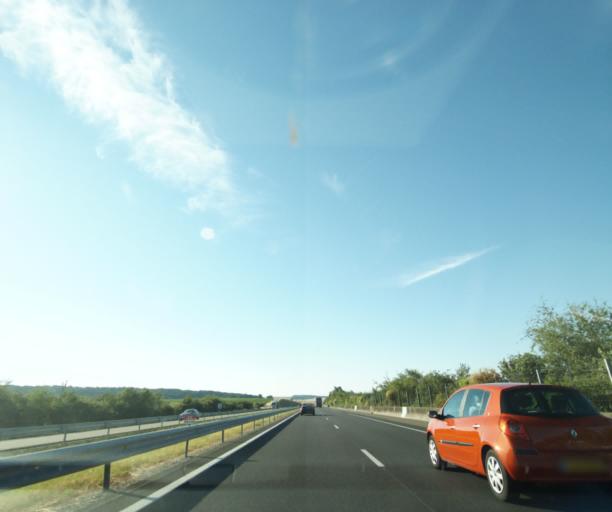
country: FR
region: Bourgogne
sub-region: Departement de l'Yonne
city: Sergines
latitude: 48.3013
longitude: 3.2546
